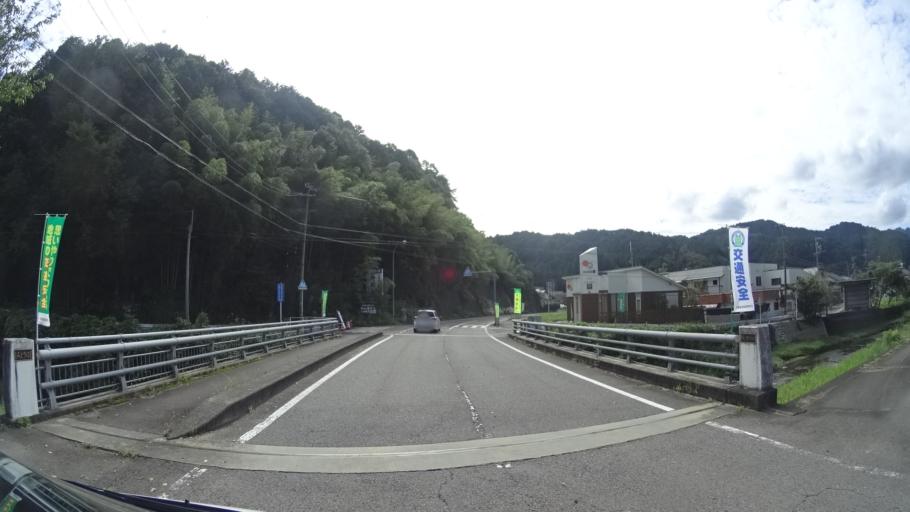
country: JP
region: Gifu
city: Minokamo
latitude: 35.5786
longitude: 137.0892
